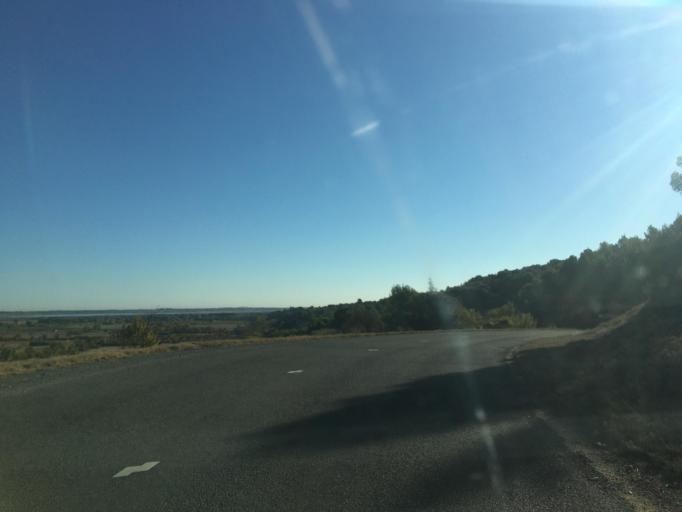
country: FR
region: Languedoc-Roussillon
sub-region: Departement de l'Aude
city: Fleury
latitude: 43.2354
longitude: 3.1696
